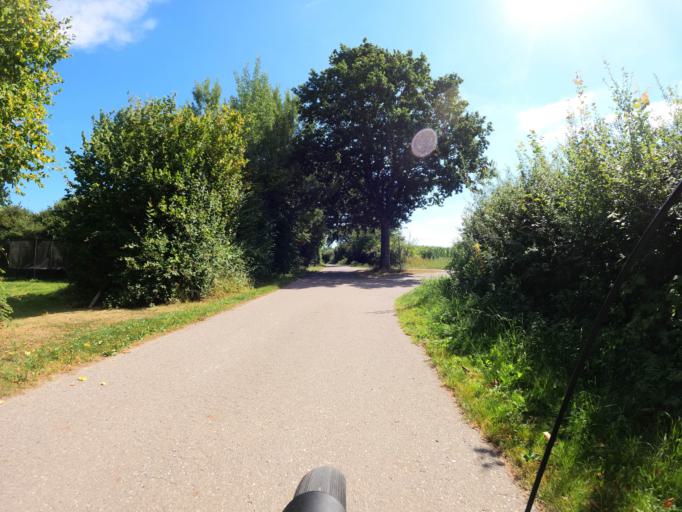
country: DE
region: Schleswig-Holstein
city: Dollerup
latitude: 54.7776
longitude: 9.6902
